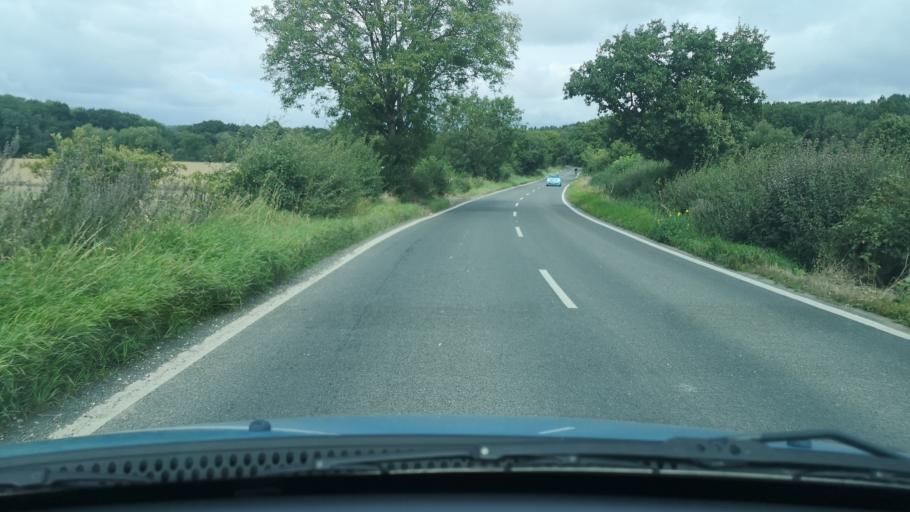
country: GB
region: England
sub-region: Barnsley
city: Royston
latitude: 53.6244
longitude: -1.4509
